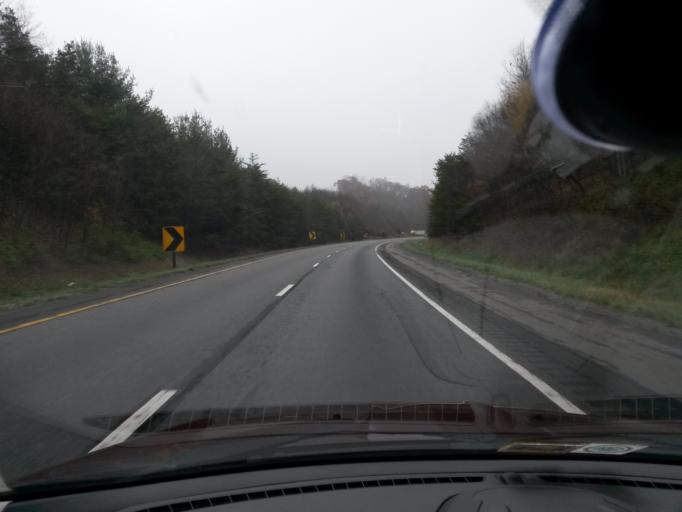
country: US
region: Virginia
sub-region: Carroll County
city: Woodlawn
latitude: 36.8102
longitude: -80.8545
